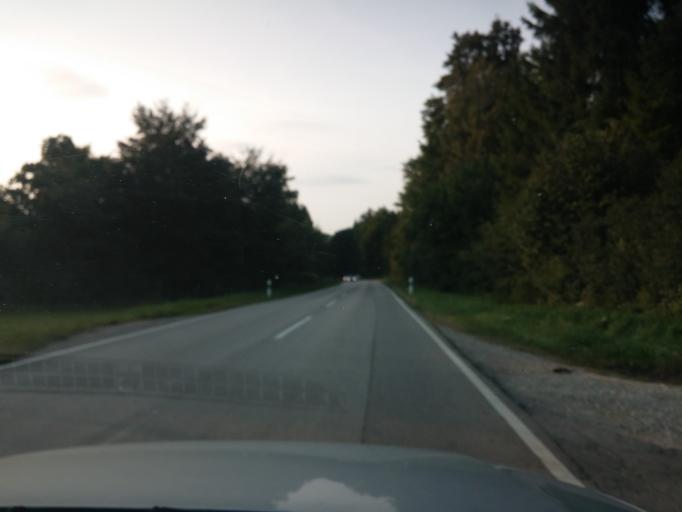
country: DE
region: Bavaria
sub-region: Upper Bavaria
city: Oberpframmern
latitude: 48.0291
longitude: 11.7962
